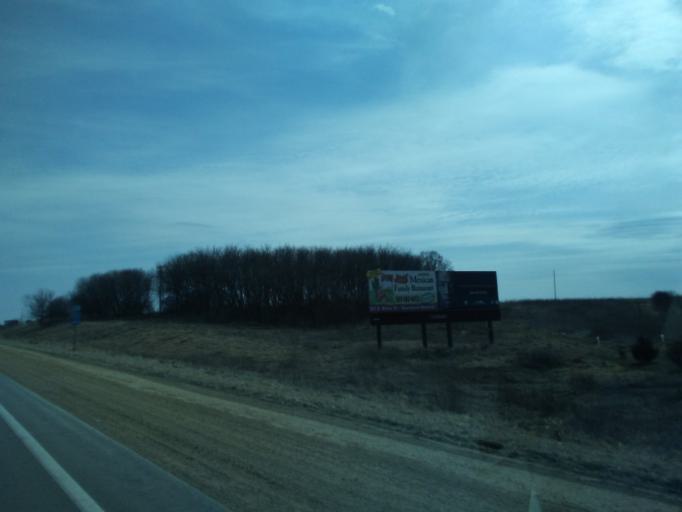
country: US
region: Iowa
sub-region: Winneshiek County
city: Decorah
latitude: 43.3705
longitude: -91.8096
